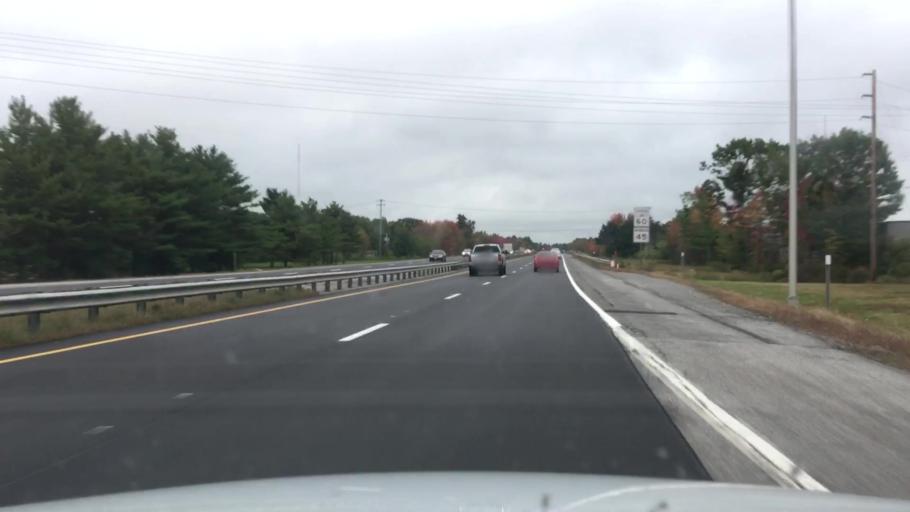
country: US
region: Maine
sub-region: Cumberland County
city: South Portland Gardens
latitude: 43.6842
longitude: -70.3234
